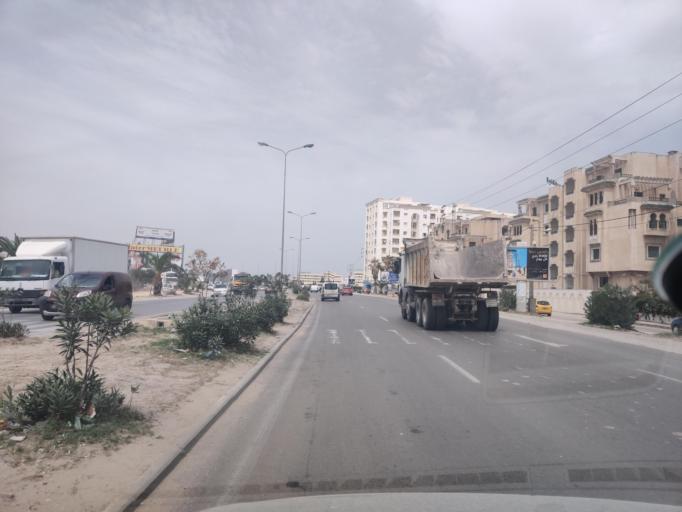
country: TN
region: Susah
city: Hammam Sousse
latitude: 35.8315
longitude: 10.5904
